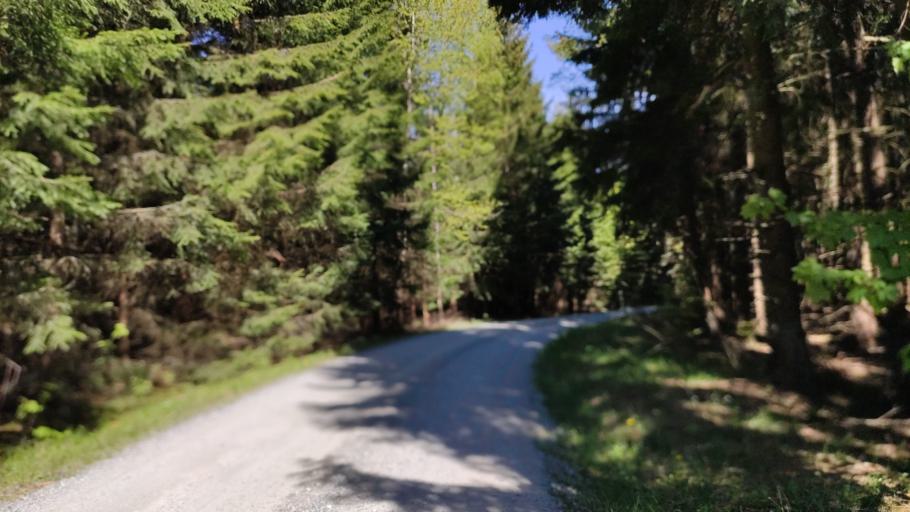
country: DE
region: Bavaria
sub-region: Upper Franconia
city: Reichenbach
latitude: 50.4572
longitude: 11.4295
